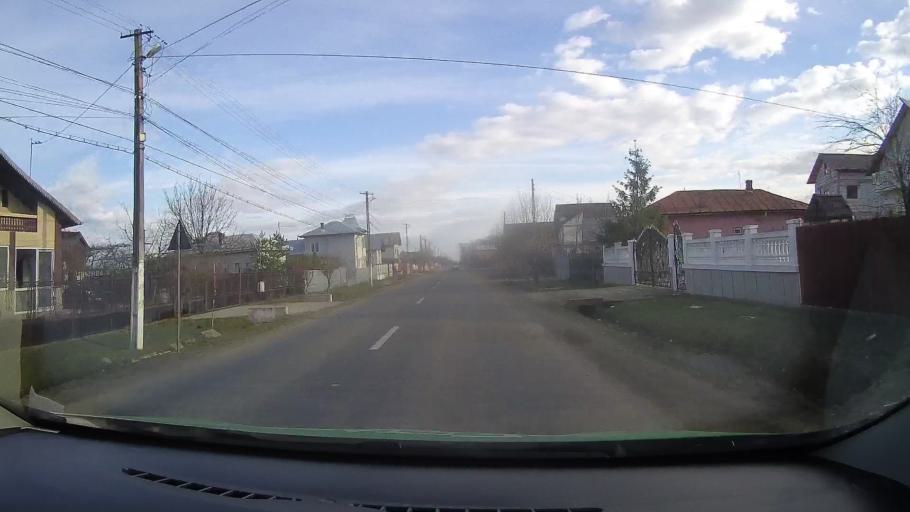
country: RO
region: Dambovita
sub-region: Comuna Vacaresti
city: Vacaresti
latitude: 44.8615
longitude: 25.4792
